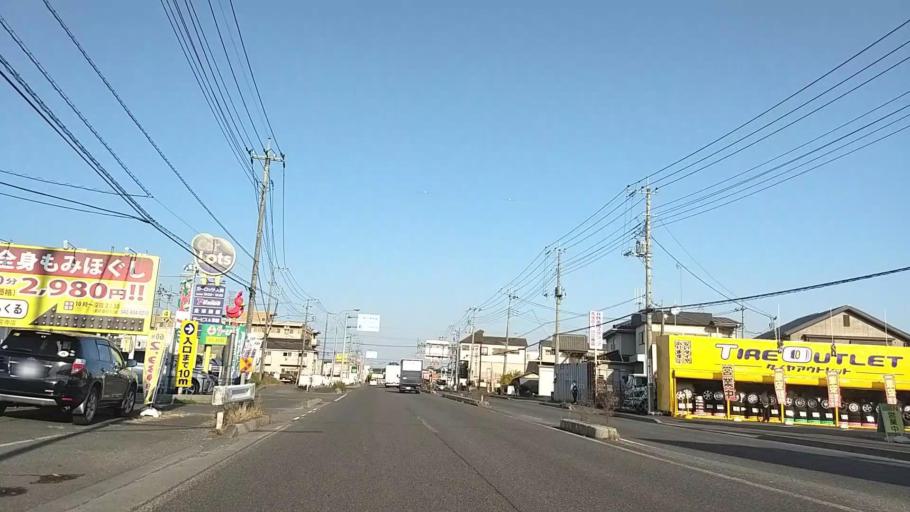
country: JP
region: Saitama
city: Sayama
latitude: 35.7996
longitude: 139.3694
